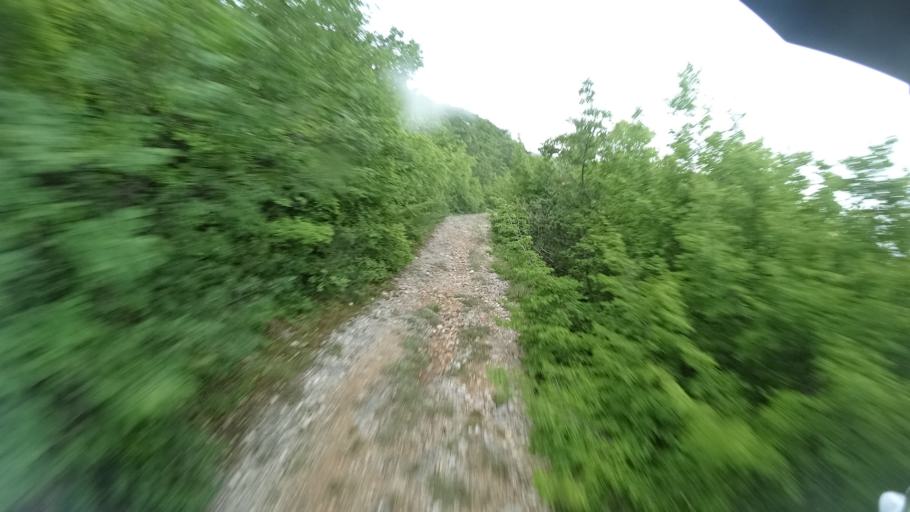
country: HR
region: Sibensko-Kniniska
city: Knin
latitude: 44.0329
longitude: 16.2300
